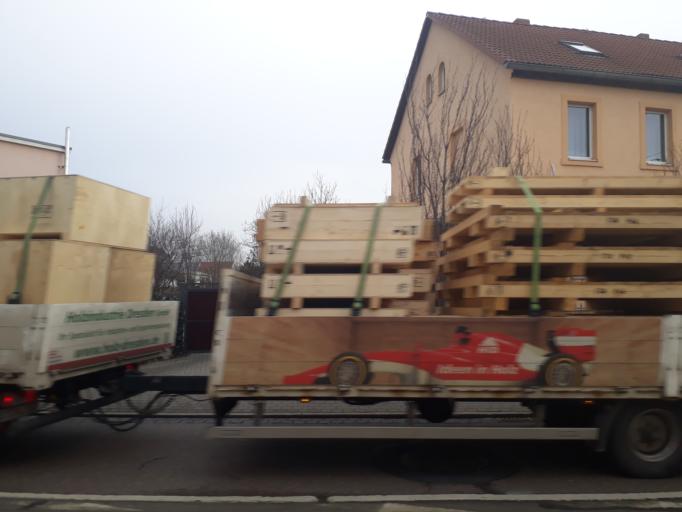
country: DE
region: Saxony
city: Heidenau
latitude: 51.0202
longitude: 13.8119
